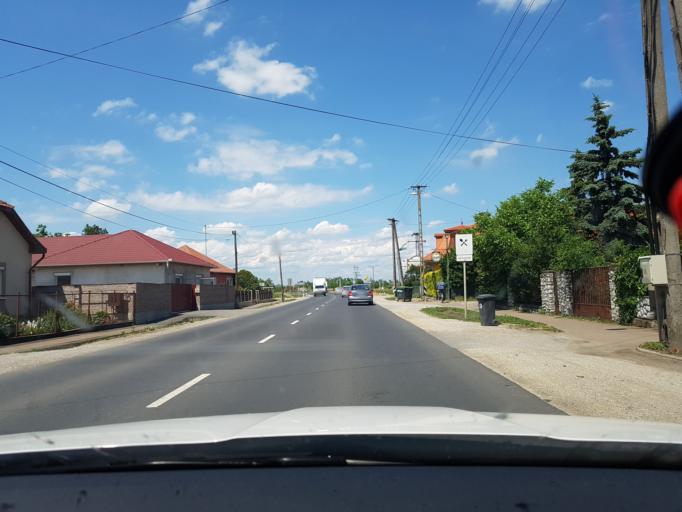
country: HU
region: Heves
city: Fuzesabony
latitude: 47.7252
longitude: 20.4169
